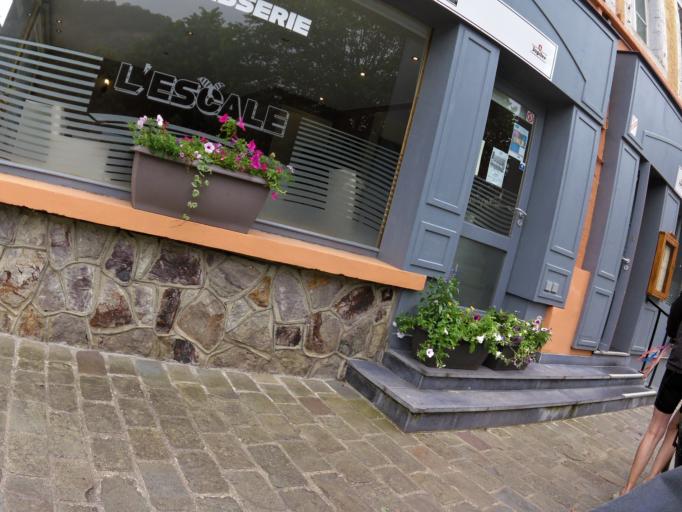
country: FR
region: Champagne-Ardenne
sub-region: Departement des Ardennes
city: Fumay
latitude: 49.9947
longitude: 4.7058
